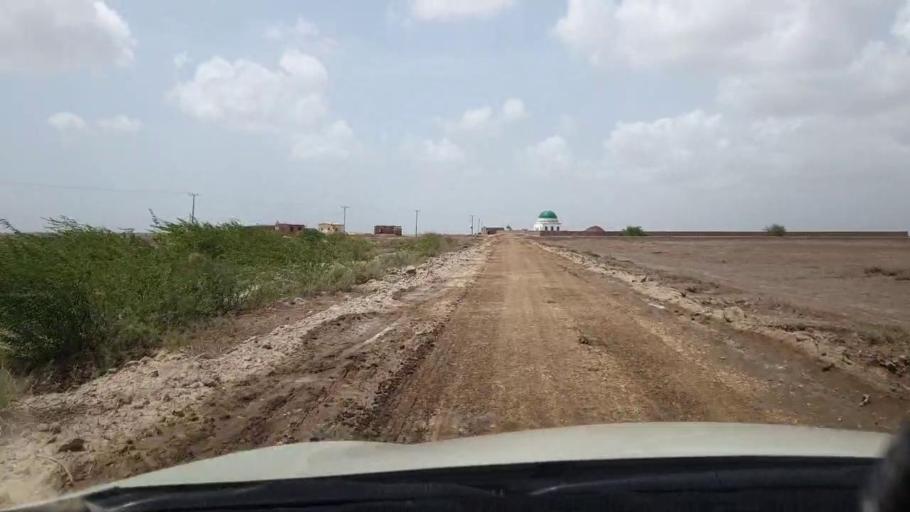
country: PK
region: Sindh
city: Kadhan
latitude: 24.3623
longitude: 68.8474
